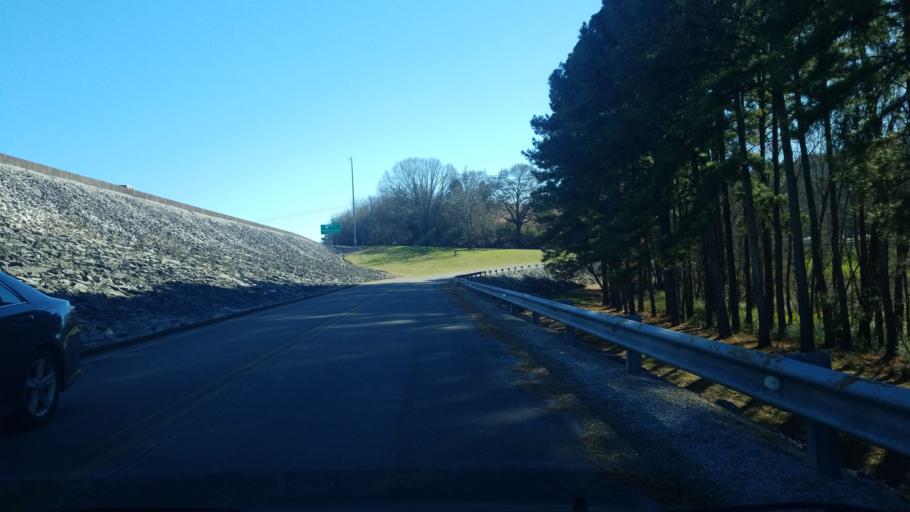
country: US
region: Tennessee
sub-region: Hamilton County
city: East Chattanooga
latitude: 35.0963
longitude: -85.2268
